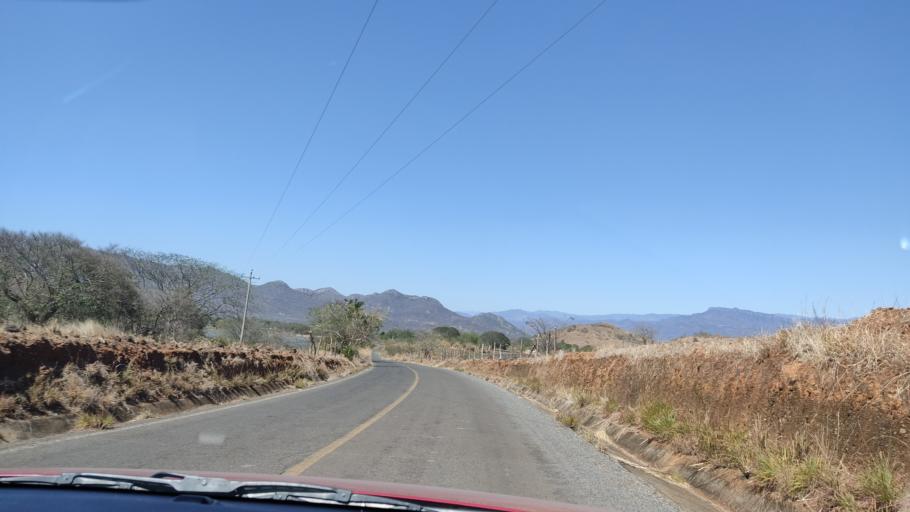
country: MX
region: Nayarit
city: Santa Maria del Oro
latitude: 21.4916
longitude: -104.6230
